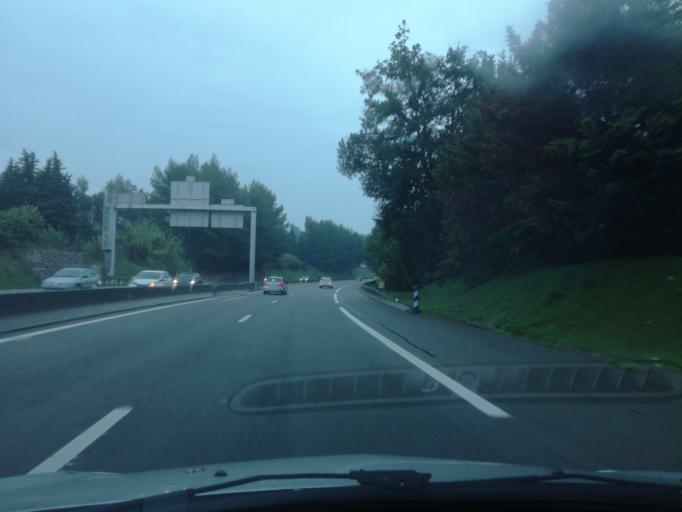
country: FR
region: Provence-Alpes-Cote d'Azur
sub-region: Departement des Alpes-Maritimes
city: Mougins
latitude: 43.5942
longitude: 7.0000
